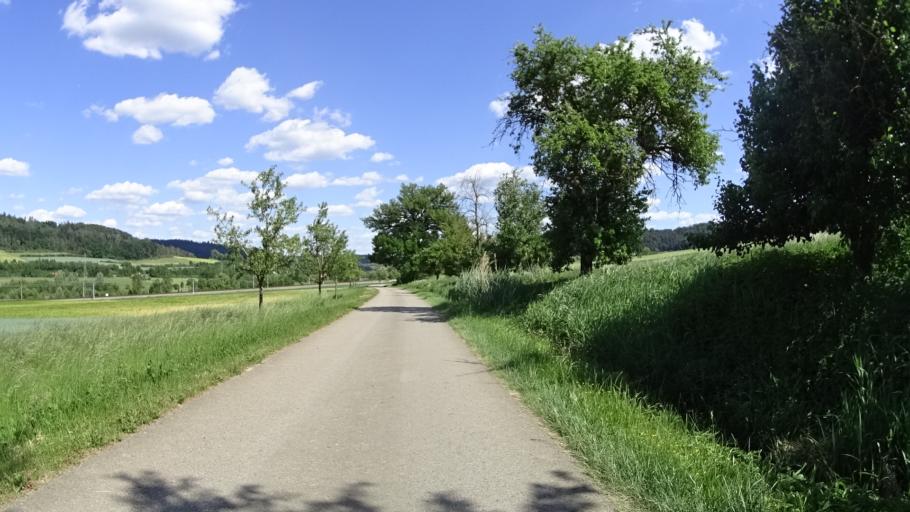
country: DE
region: Bavaria
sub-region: Regierungsbezirk Mittelfranken
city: Greding
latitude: 49.0695
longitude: 11.2959
